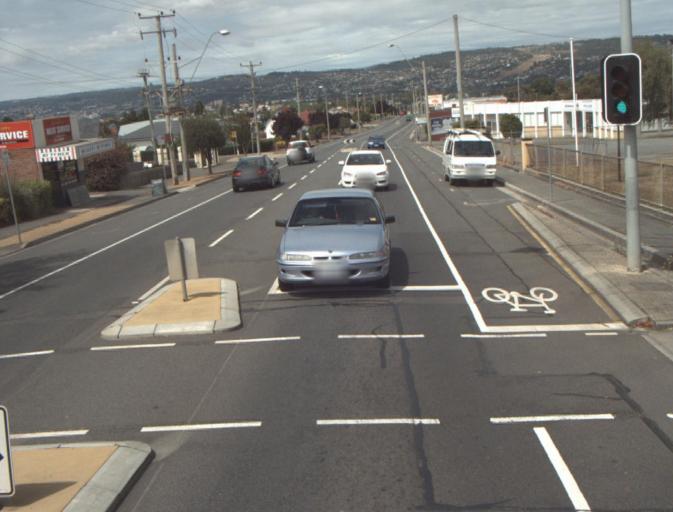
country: AU
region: Tasmania
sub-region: Launceston
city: Mayfield
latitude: -41.3856
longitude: 147.1277
